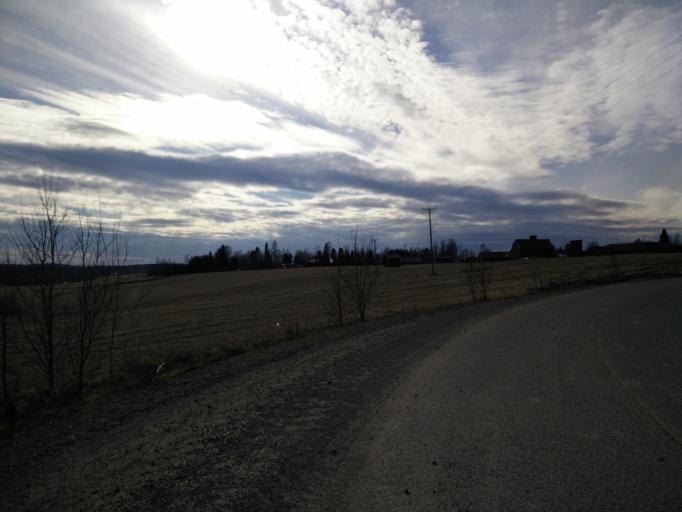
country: FI
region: Pirkanmaa
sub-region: Tampere
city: Orivesi
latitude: 61.7083
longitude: 24.3338
